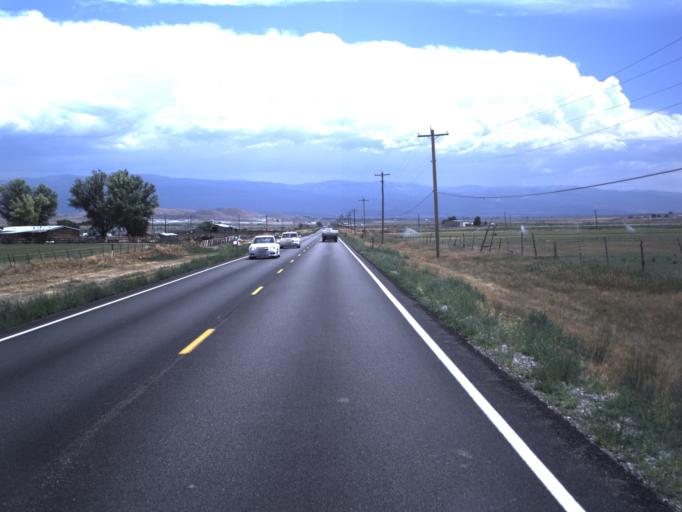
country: US
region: Utah
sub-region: Sanpete County
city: Fountain Green
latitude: 39.6010
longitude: -111.6220
